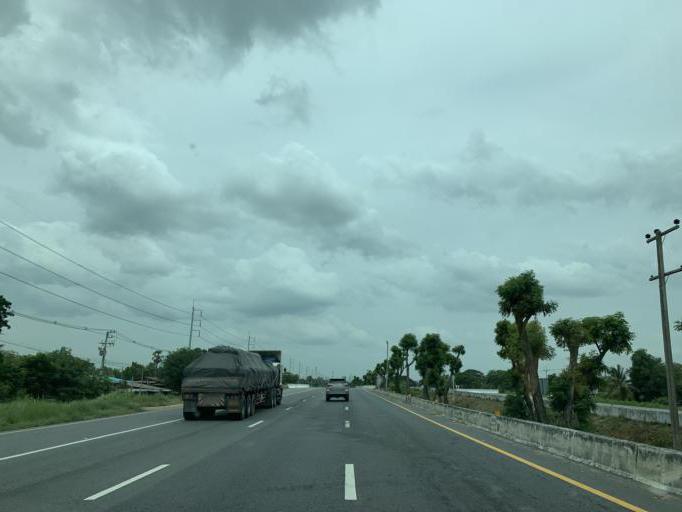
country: TH
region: Sing Buri
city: In Buri
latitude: 15.0599
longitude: 100.3244
